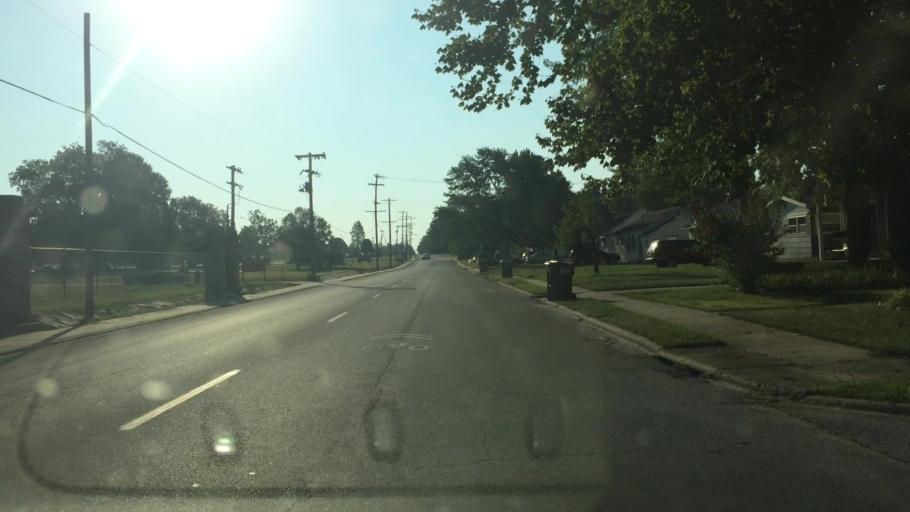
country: US
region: Missouri
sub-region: Greene County
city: Springfield
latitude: 37.2185
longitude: -93.2692
